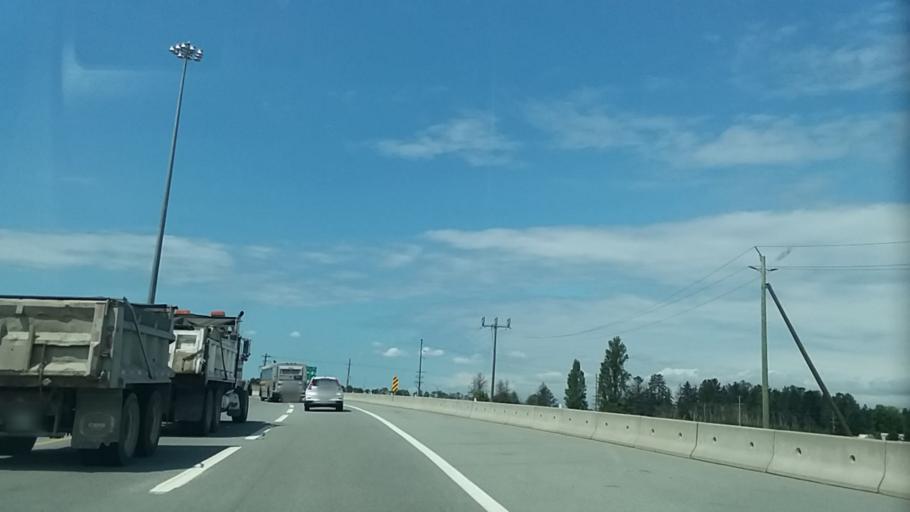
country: CA
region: British Columbia
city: Ladner
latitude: 49.0952
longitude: -123.0223
